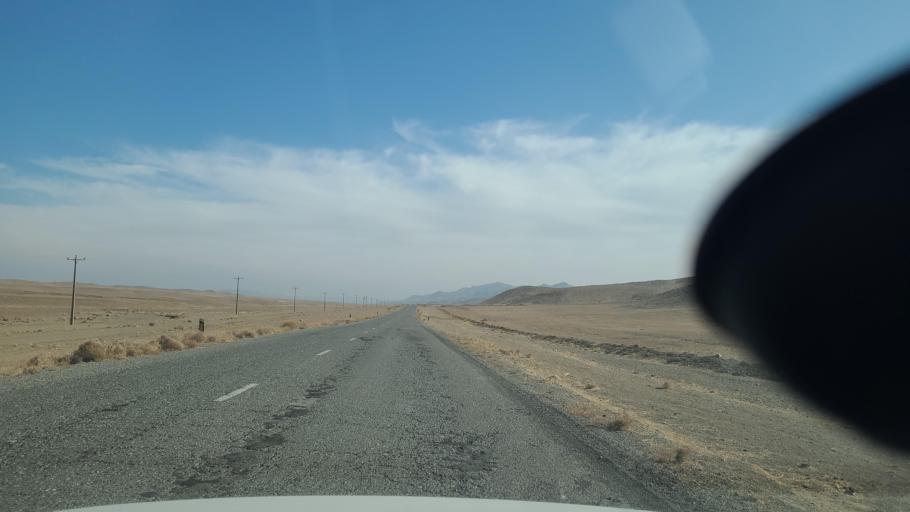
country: IR
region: Razavi Khorasan
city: Fariman
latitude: 35.5910
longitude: 59.6099
